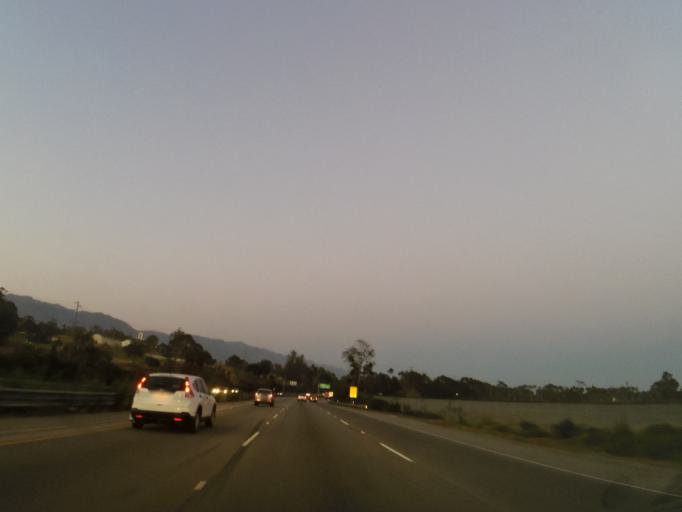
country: US
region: California
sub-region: Santa Barbara County
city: Montecito
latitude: 34.4223
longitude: -119.6625
